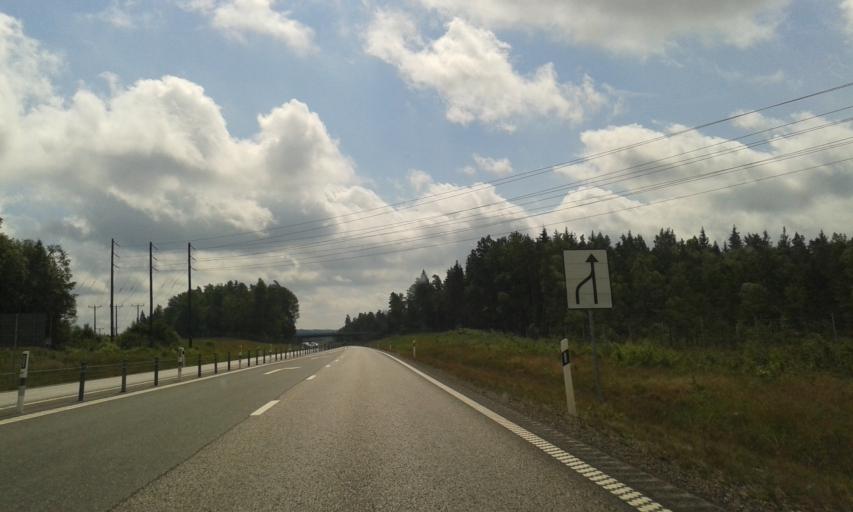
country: SE
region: Joenkoeping
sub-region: Gislaveds Kommun
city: Gislaved
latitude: 57.2935
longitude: 13.5915
